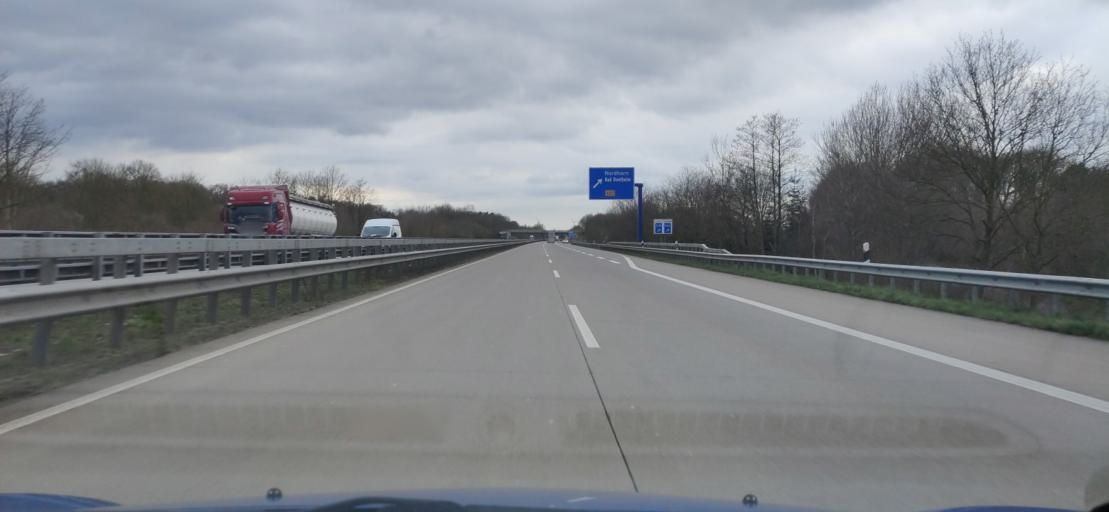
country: DE
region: Lower Saxony
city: Isterberg
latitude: 52.3396
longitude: 7.1581
